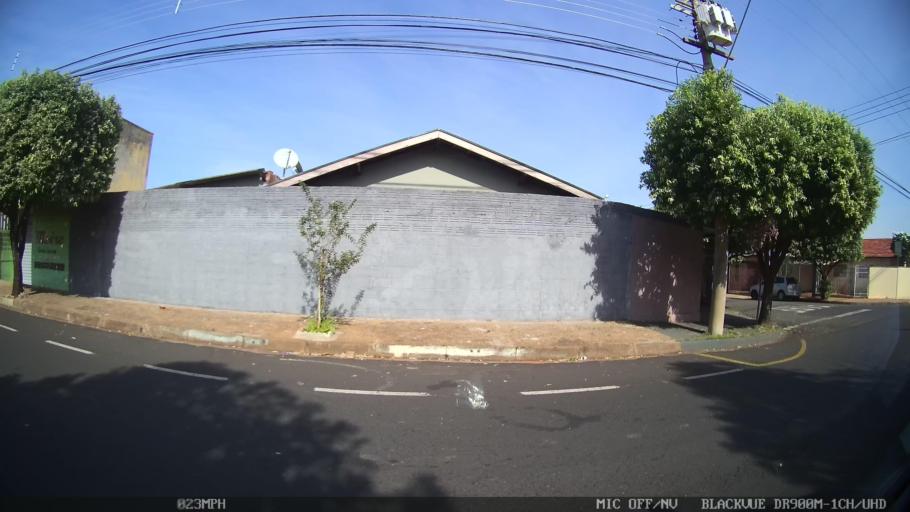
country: BR
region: Sao Paulo
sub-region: Sao Jose Do Rio Preto
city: Sao Jose do Rio Preto
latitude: -20.7966
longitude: -49.4200
